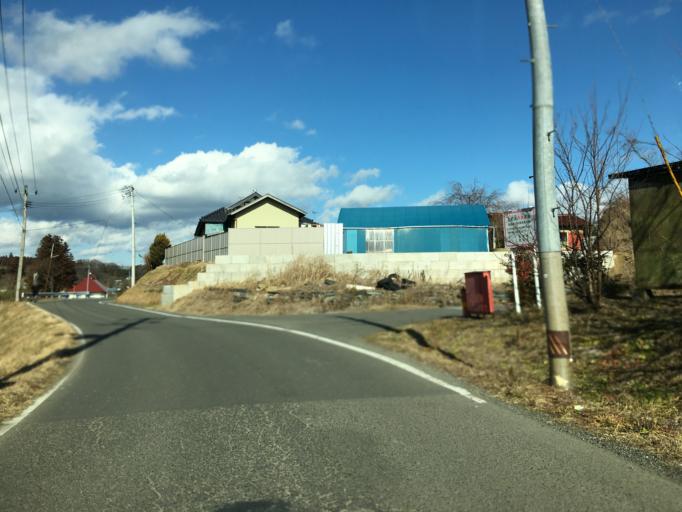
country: JP
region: Fukushima
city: Funehikimachi-funehiki
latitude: 37.4361
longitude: 140.5613
